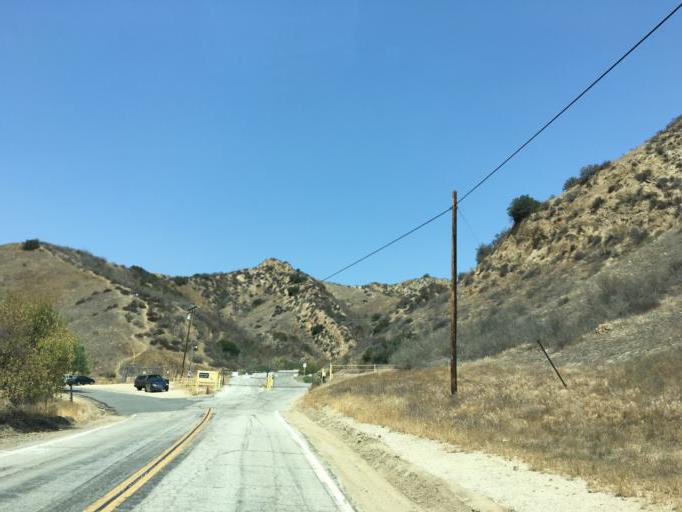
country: US
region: California
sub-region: Los Angeles County
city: Santa Clarita
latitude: 34.3809
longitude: -118.6041
